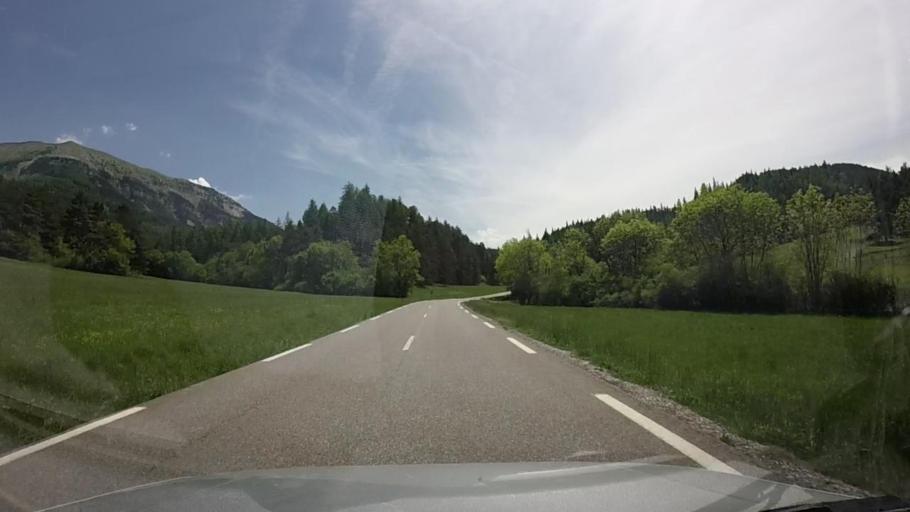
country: FR
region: Provence-Alpes-Cote d'Azur
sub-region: Departement des Alpes-de-Haute-Provence
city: Seyne-les-Alpes
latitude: 44.2551
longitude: 6.3669
